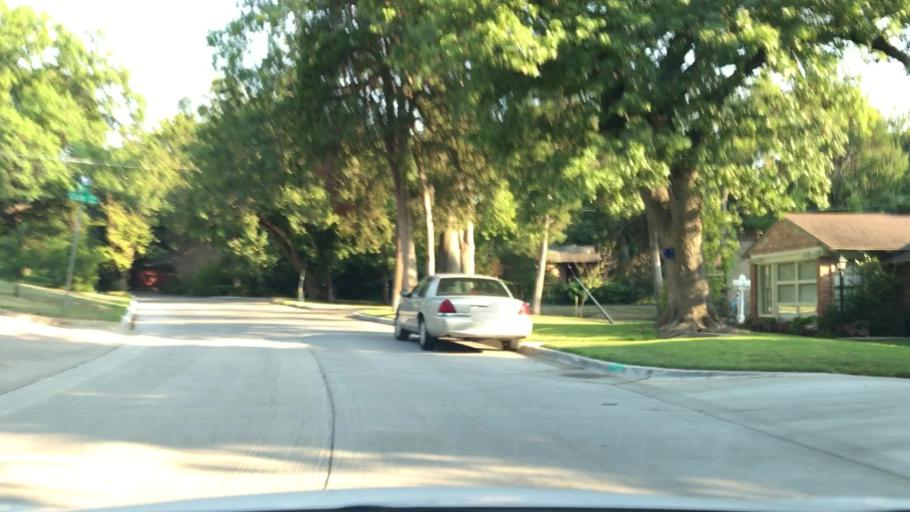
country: US
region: Texas
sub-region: Dallas County
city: Cockrell Hill
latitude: 32.7444
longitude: -96.8676
